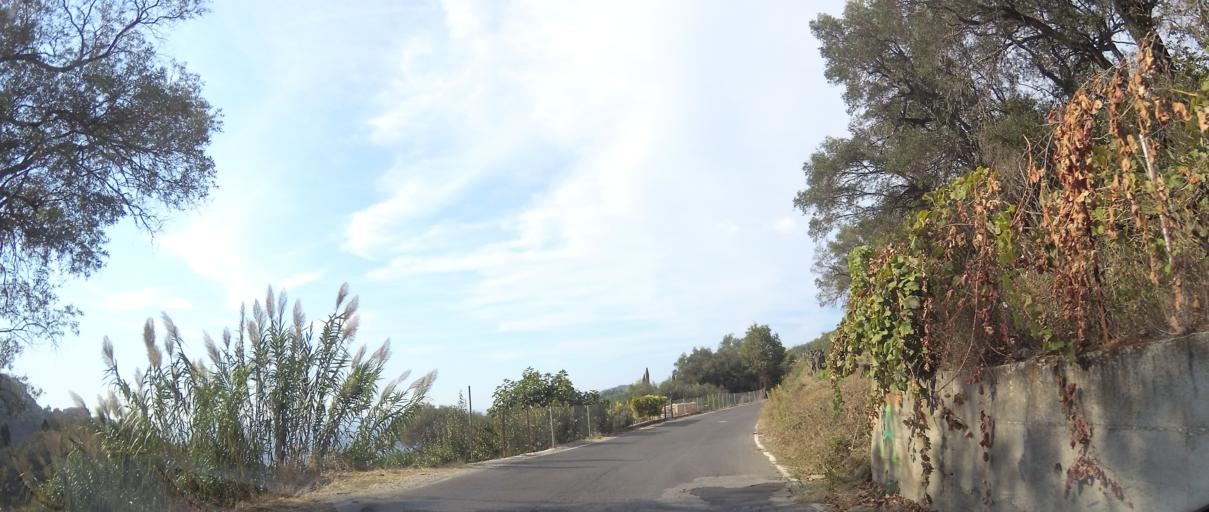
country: GR
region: Ionian Islands
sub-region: Nomos Kerkyras
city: Kynopiastes
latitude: 39.5439
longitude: 19.8693
